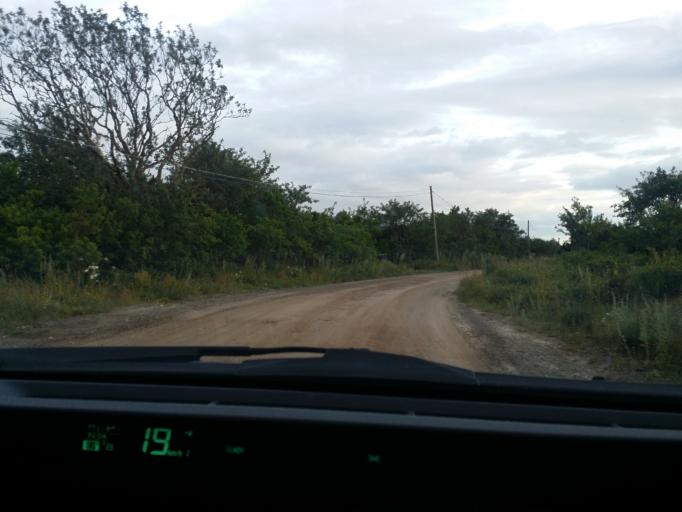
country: SE
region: Kalmar
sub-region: Borgholms Kommun
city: Borgholm
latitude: 57.2148
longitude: 16.9436
